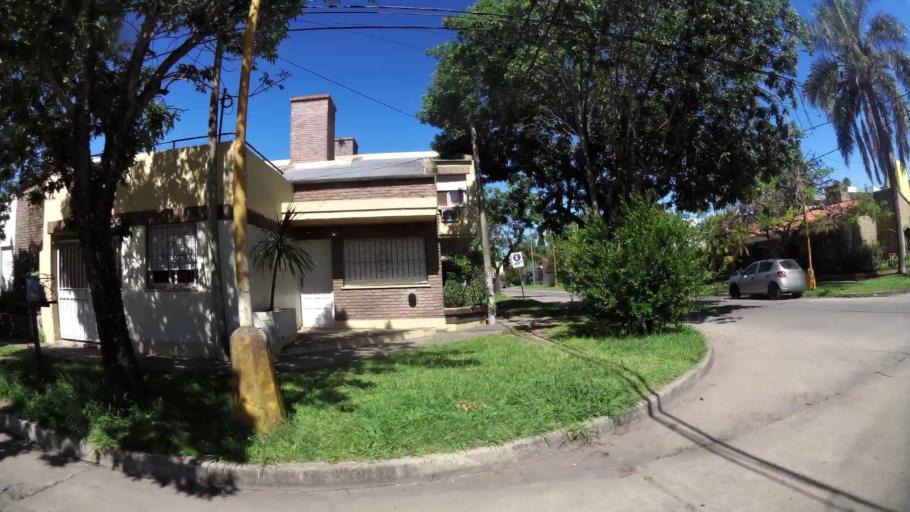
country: AR
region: Santa Fe
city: Santa Fe de la Vera Cruz
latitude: -31.6057
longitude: -60.6716
